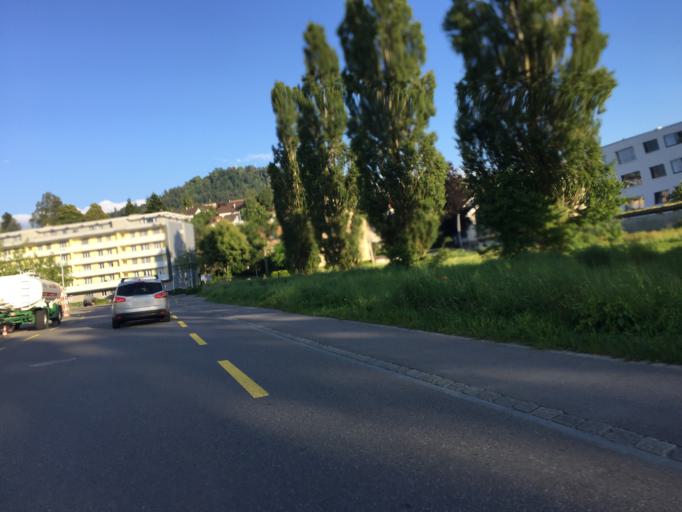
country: CH
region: Bern
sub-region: Bern-Mittelland District
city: Koniz
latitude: 46.9291
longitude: 7.4224
